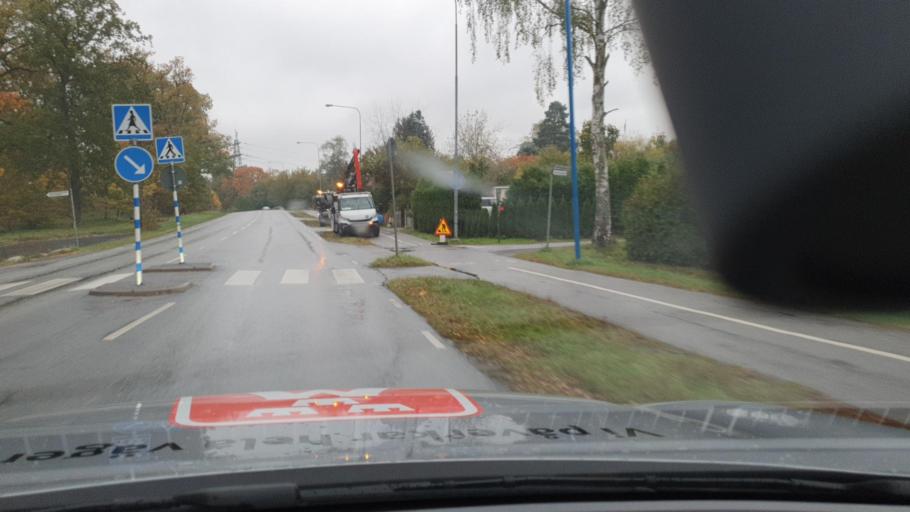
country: SE
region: Stockholm
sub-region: Osterakers Kommun
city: Akersberga
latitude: 59.4900
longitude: 18.2865
